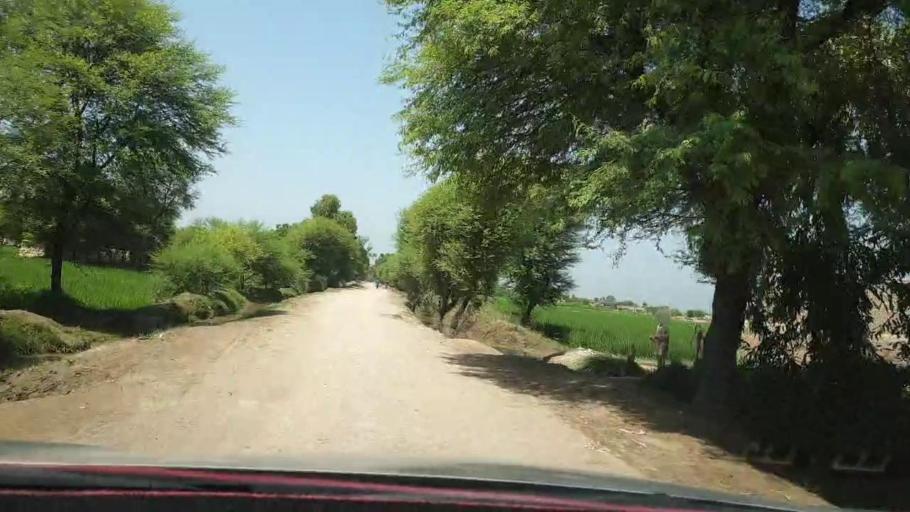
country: PK
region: Sindh
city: Warah
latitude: 27.5239
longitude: 67.8138
